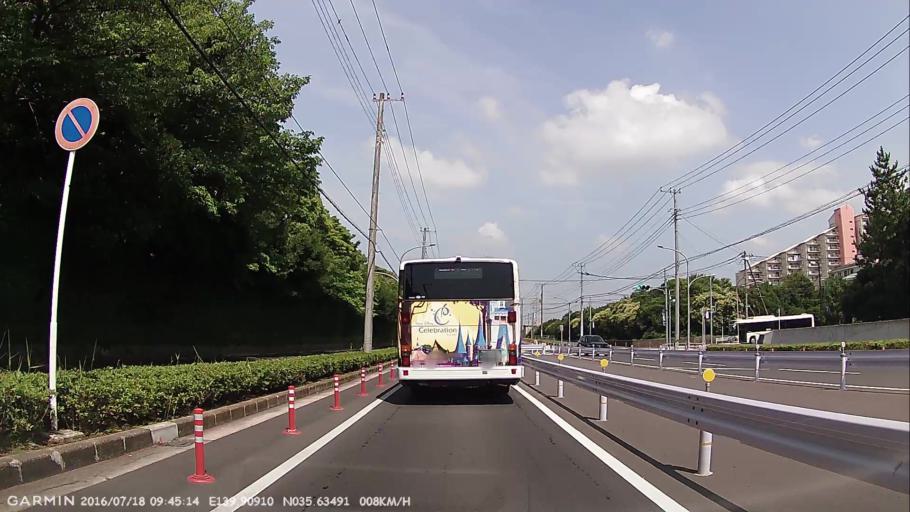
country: JP
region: Tokyo
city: Urayasu
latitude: 35.6349
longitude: 139.9091
